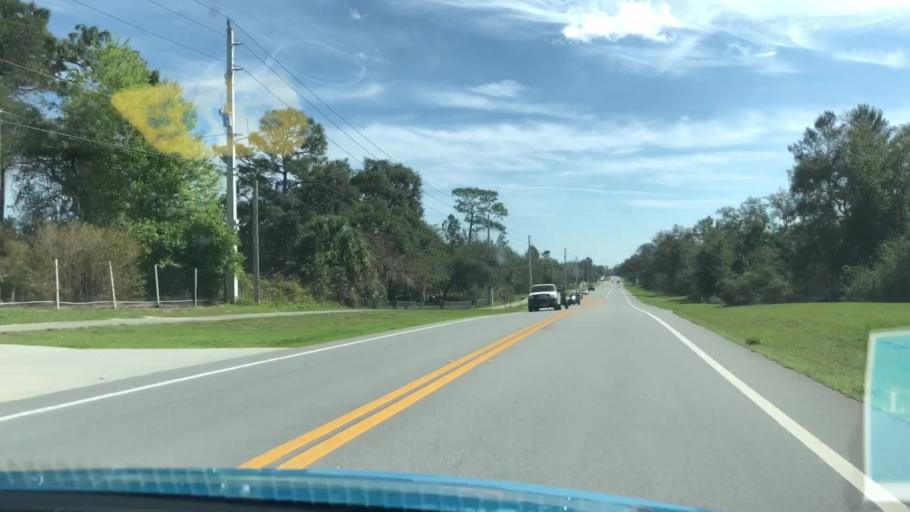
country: US
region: Florida
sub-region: Seminole County
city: Midway
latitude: 28.8547
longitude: -81.1806
